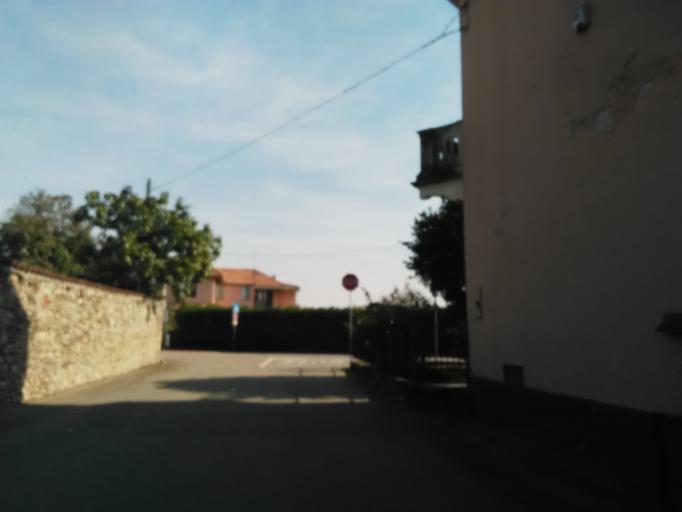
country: IT
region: Piedmont
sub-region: Provincia di Vercelli
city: Lenta
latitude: 45.5533
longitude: 8.3841
